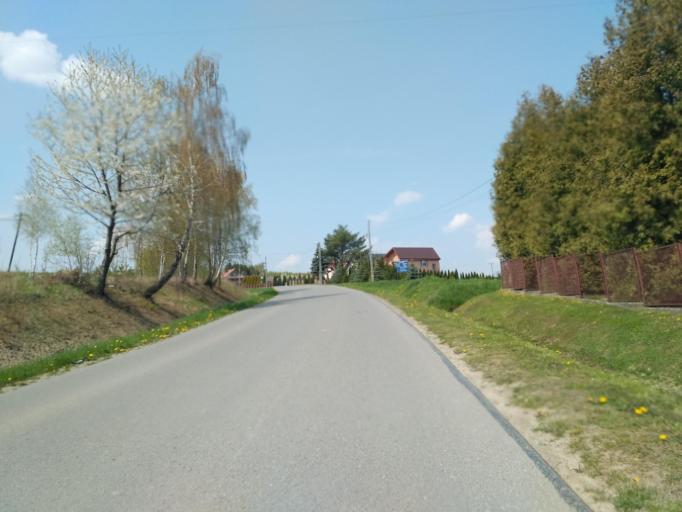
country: PL
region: Subcarpathian Voivodeship
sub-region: Powiat jasielski
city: Tarnowiec
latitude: 49.6704
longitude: 21.5564
